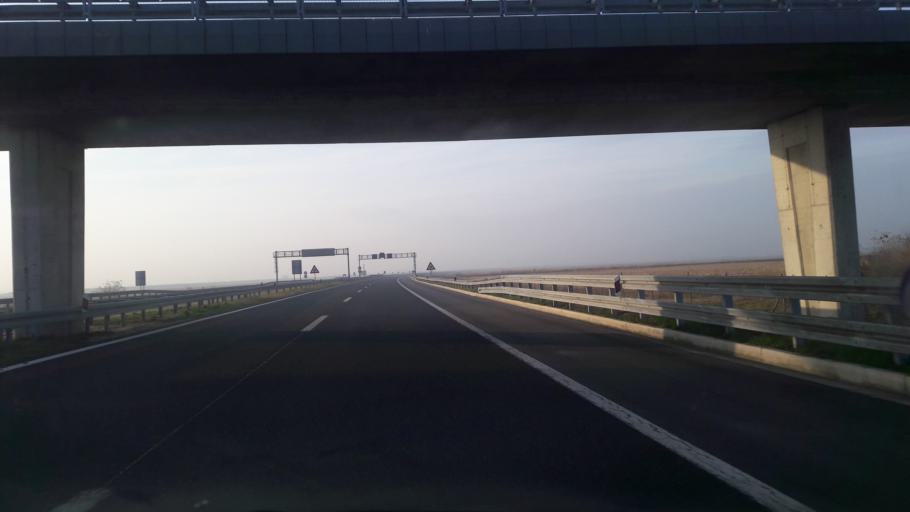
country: HR
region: Osjecko-Baranjska
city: Josipovac
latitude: 45.5671
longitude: 18.5489
